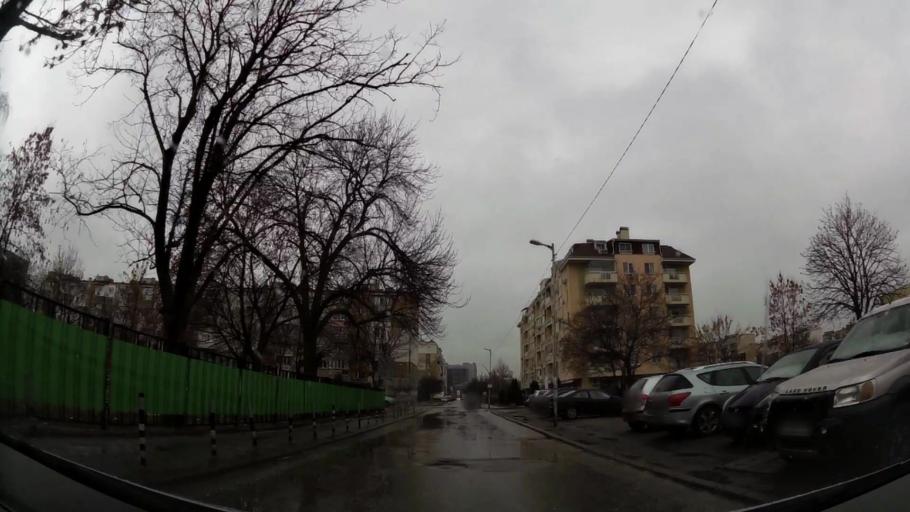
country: BG
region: Sofia-Capital
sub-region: Stolichna Obshtina
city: Sofia
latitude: 42.6646
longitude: 23.3959
